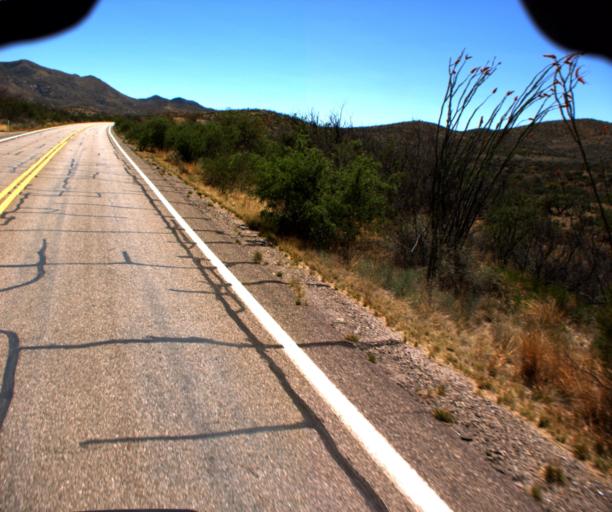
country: US
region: Arizona
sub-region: Pima County
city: Corona de Tucson
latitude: 31.9303
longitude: -110.6587
